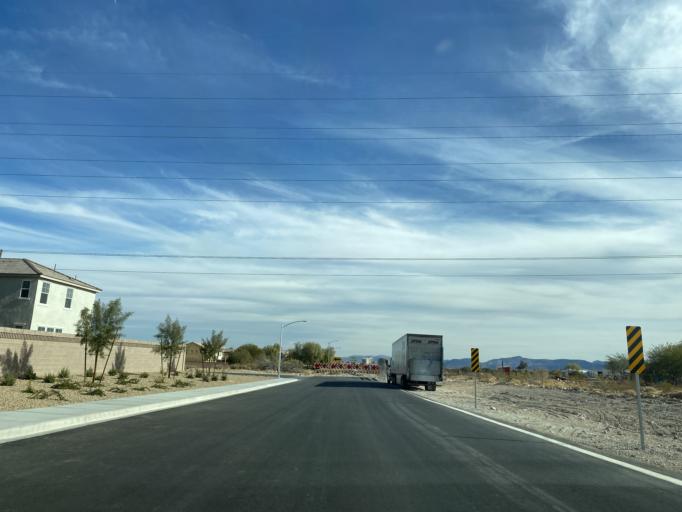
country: US
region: Nevada
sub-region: Clark County
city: Enterprise
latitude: 36.0406
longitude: -115.2132
